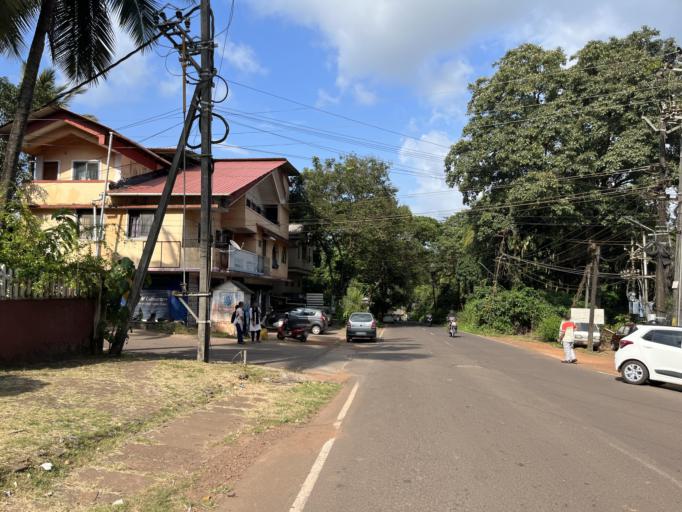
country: IN
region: Goa
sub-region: North Goa
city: Ponda
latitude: 15.4041
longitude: 74.0155
